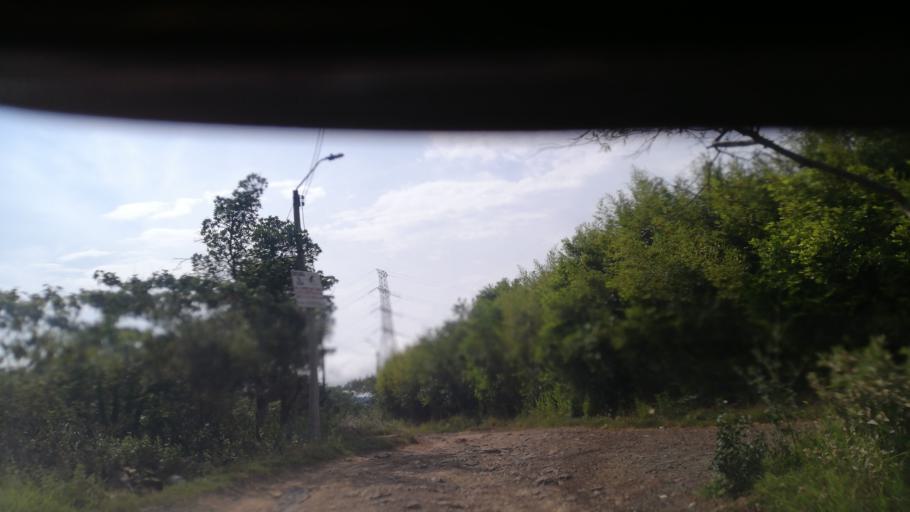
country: CO
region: Valle del Cauca
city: Cali
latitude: 3.4956
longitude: -76.5444
